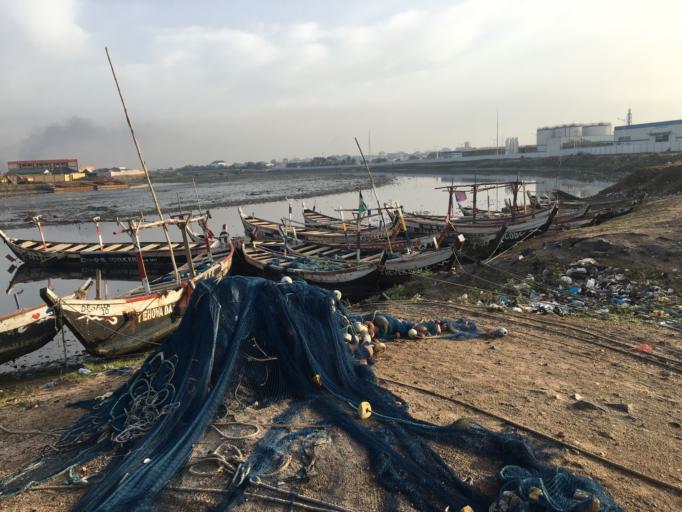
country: GH
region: Greater Accra
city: Accra
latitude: 5.5313
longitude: -0.2200
